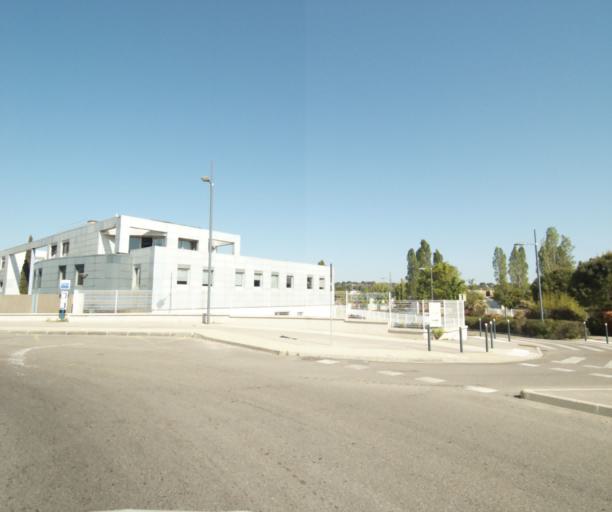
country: FR
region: Languedoc-Roussillon
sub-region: Departement de l'Herault
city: Castelnau-le-Lez
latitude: 43.6258
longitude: 3.9064
